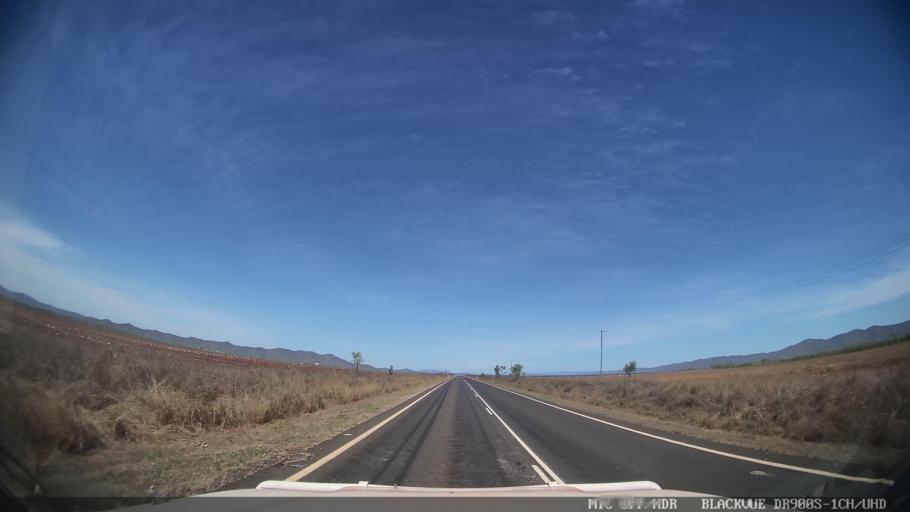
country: AU
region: Queensland
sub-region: Cook
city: Cooktown
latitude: -15.7931
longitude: 144.7105
